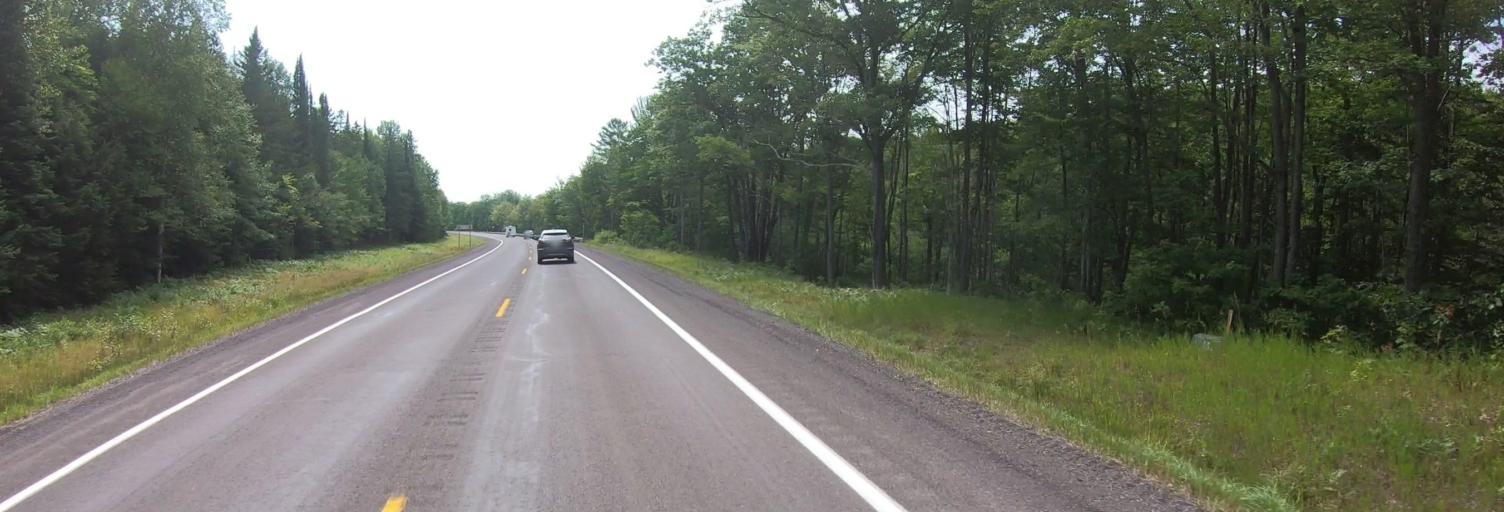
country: US
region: Michigan
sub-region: Houghton County
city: Hancock
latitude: 46.9129
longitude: -88.8257
